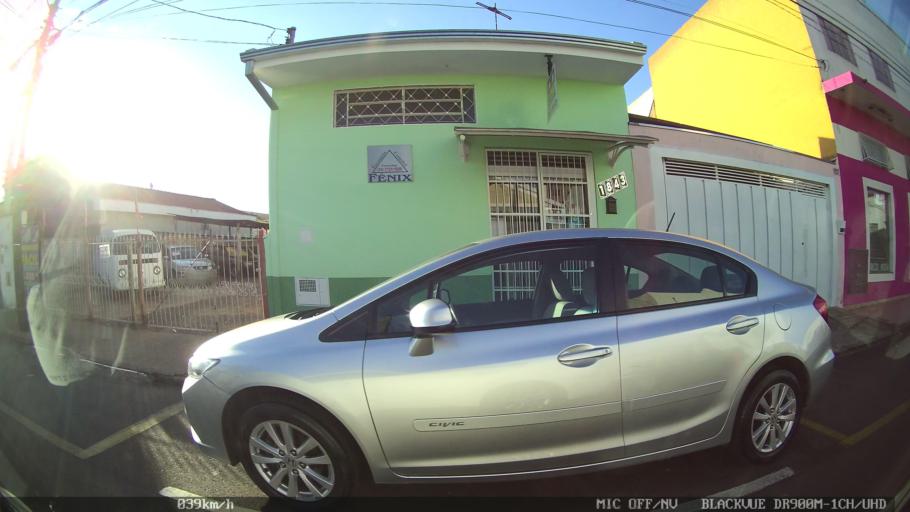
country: BR
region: Sao Paulo
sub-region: Franca
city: Franca
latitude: -20.5250
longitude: -47.3741
